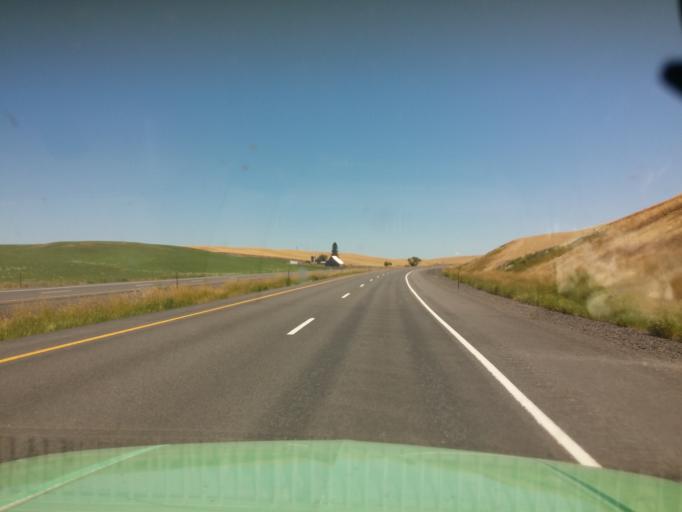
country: US
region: Idaho
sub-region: Nez Perce County
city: Lewiston
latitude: 46.5091
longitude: -116.9793
